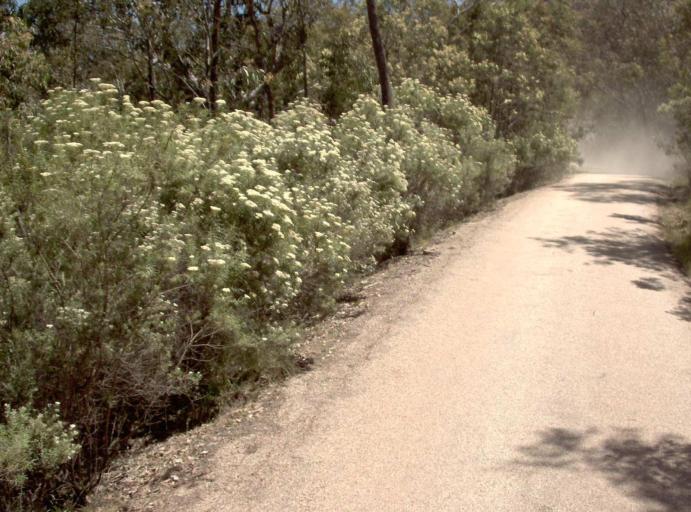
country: AU
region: New South Wales
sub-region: Snowy River
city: Jindabyne
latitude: -37.0771
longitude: 148.3456
